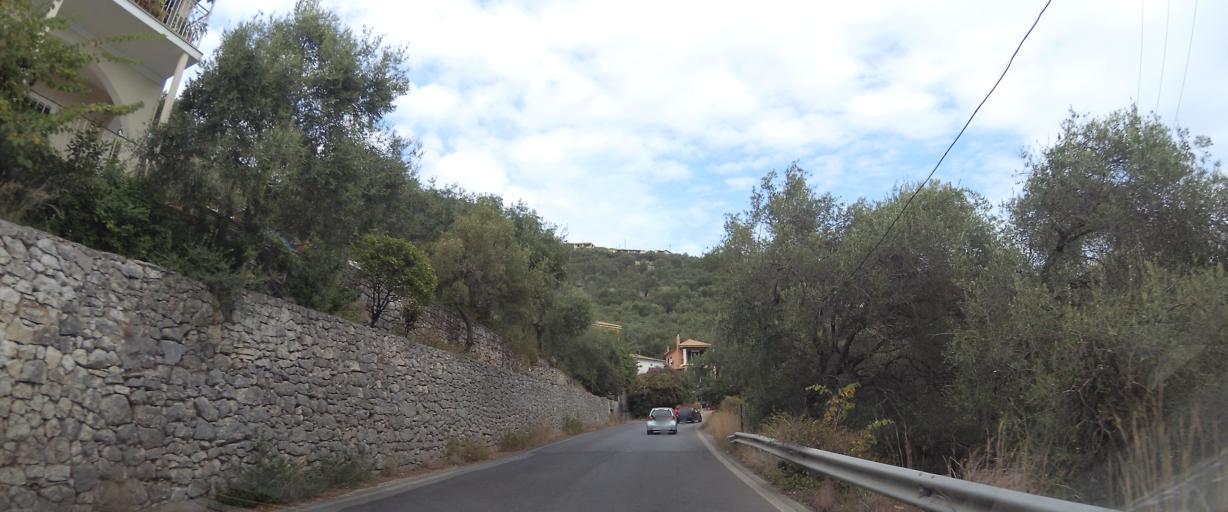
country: GR
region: Ionian Islands
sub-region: Nomos Kerkyras
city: Kontokali
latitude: 39.7266
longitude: 19.8975
